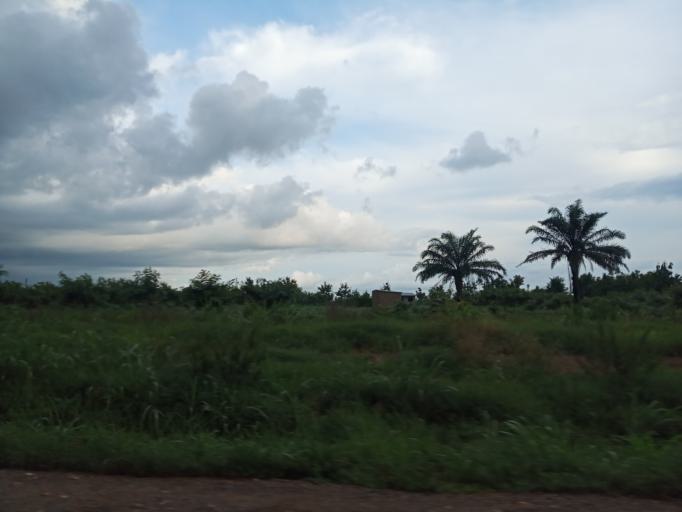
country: TG
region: Centrale
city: Sotouboua
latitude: 8.5881
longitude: 0.9905
